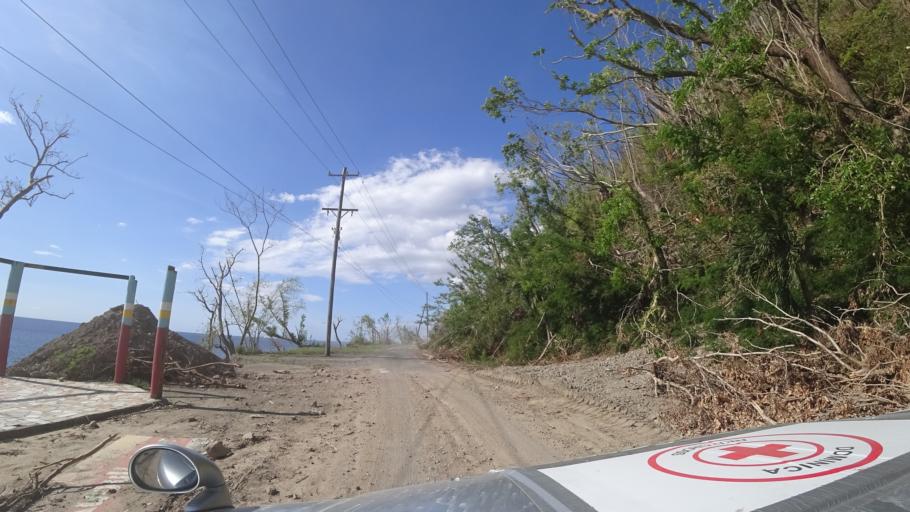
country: DM
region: Saint Luke
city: Pointe Michel
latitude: 15.2516
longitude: -61.3750
